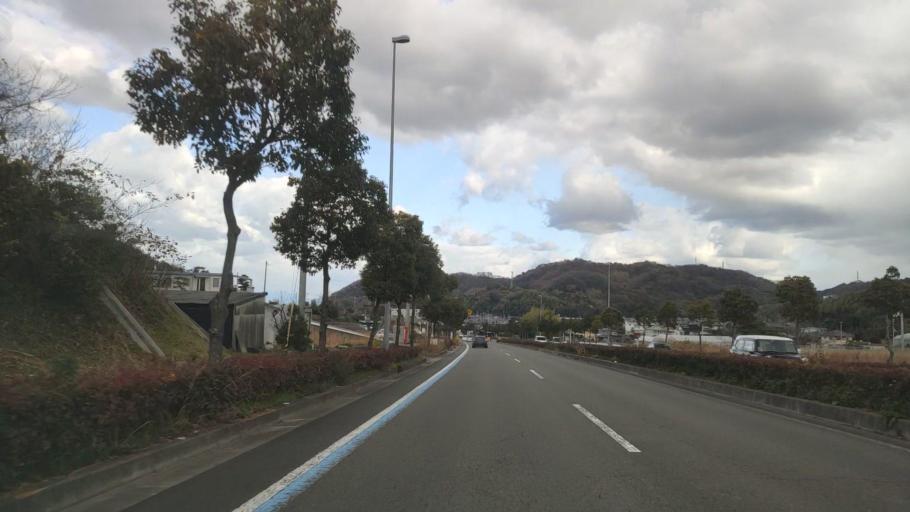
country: JP
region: Ehime
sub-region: Shikoku-chuo Shi
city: Matsuyama
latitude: 33.8938
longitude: 132.7579
